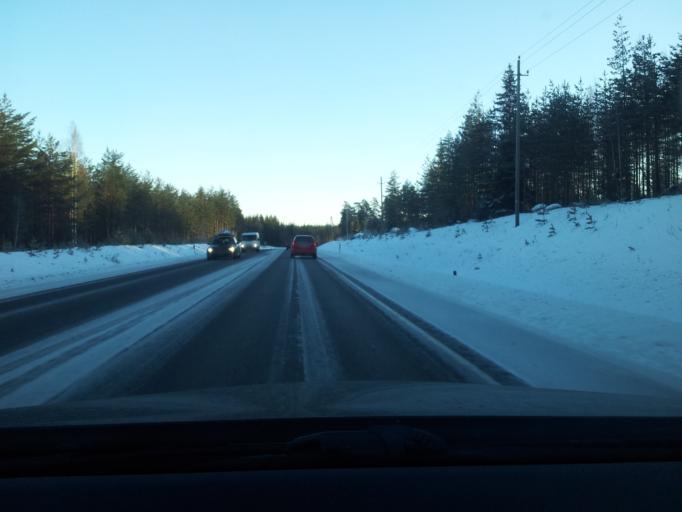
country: FI
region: Uusimaa
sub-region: Helsinki
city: Vihti
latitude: 60.3629
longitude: 24.3555
